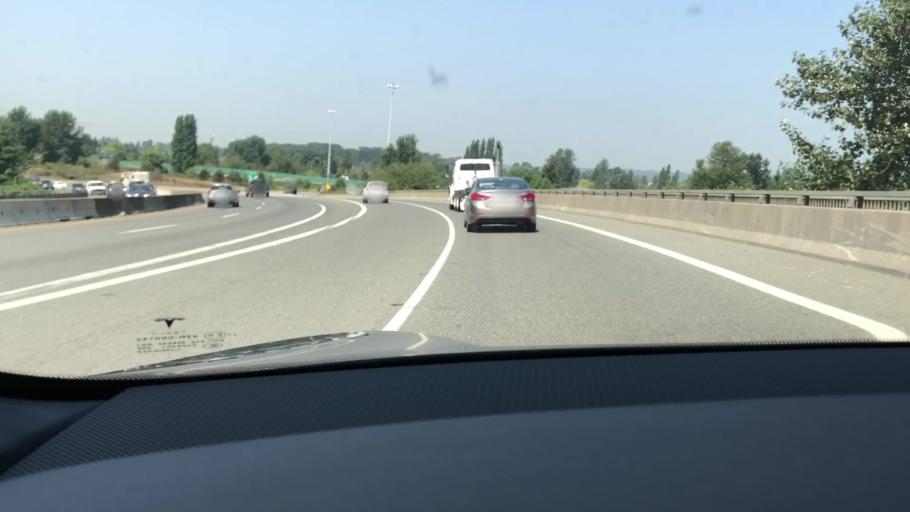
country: CA
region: British Columbia
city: New Westminster
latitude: 49.1770
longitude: -122.9567
